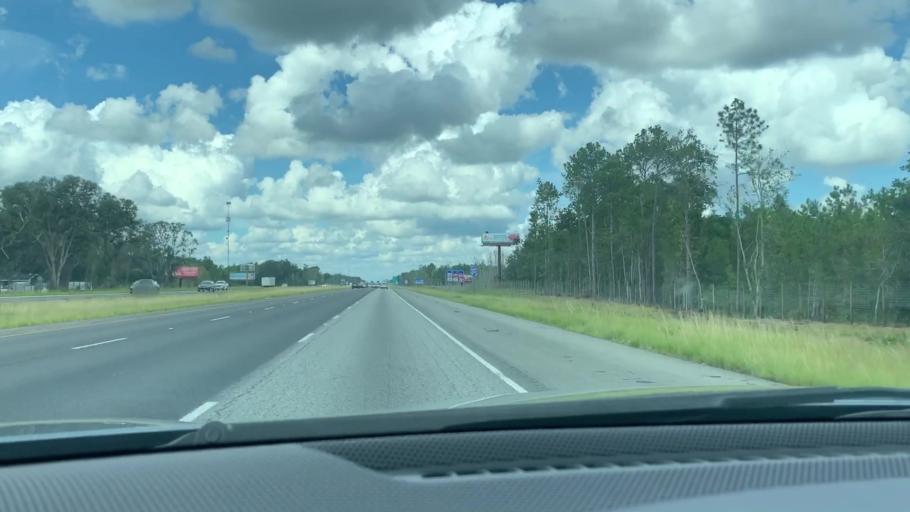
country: US
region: Georgia
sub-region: Camden County
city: Kingsland
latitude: 30.7680
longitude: -81.6539
